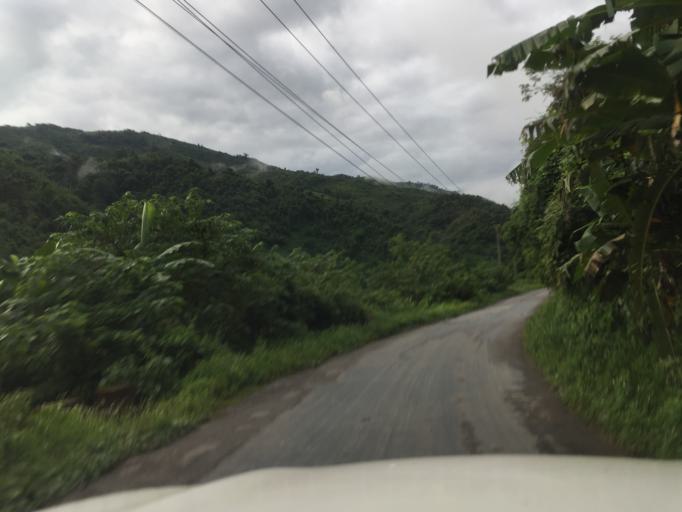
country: LA
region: Oudomxai
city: Muang La
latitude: 21.0616
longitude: 102.2405
